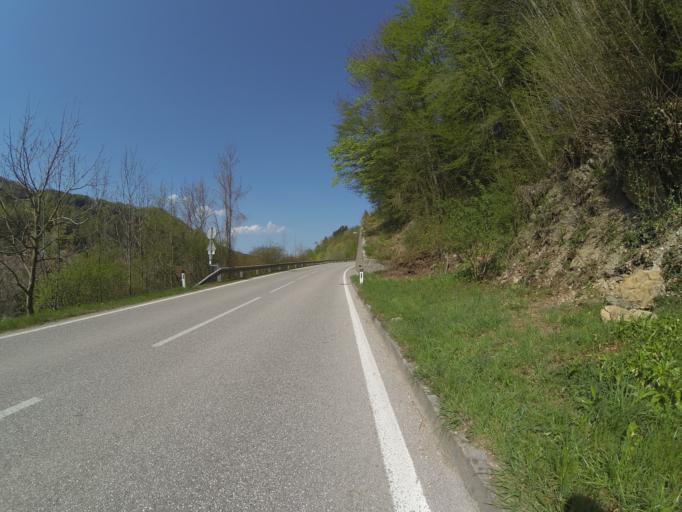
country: AT
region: Upper Austria
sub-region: Politischer Bezirk Gmunden
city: Altmunster
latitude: 47.9260
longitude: 13.7542
